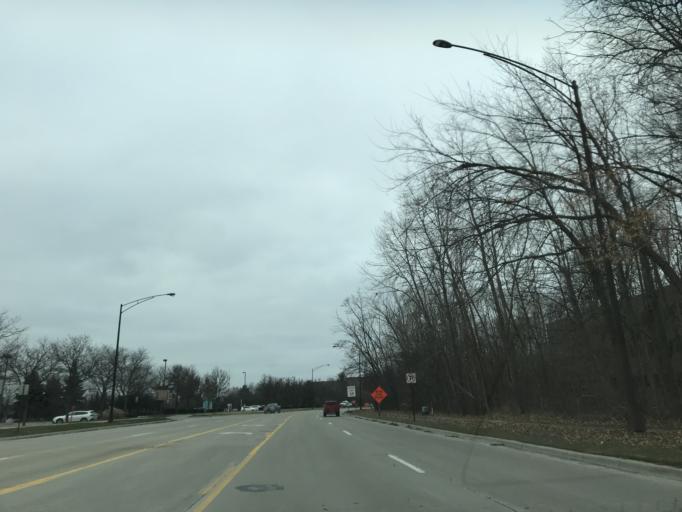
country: US
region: Michigan
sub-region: Oakland County
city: Troy
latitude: 42.5971
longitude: -83.1716
